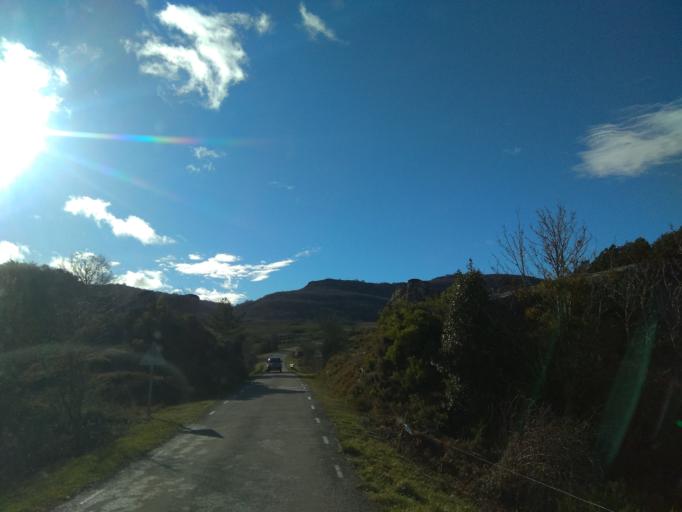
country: ES
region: Cantabria
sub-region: Provincia de Cantabria
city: San Martin de Elines
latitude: 42.9477
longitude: -3.8168
